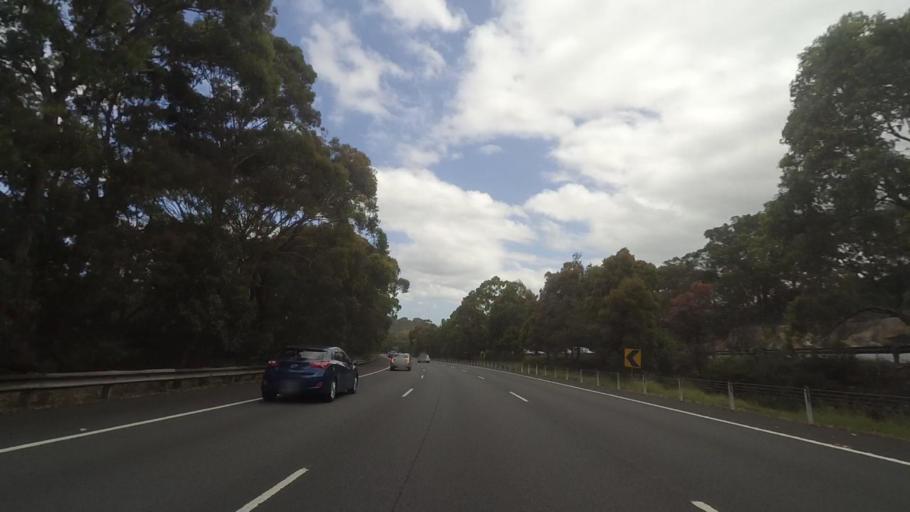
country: AU
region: New South Wales
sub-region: Hornsby Shire
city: Berowra Heights
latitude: -33.5049
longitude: 151.1890
